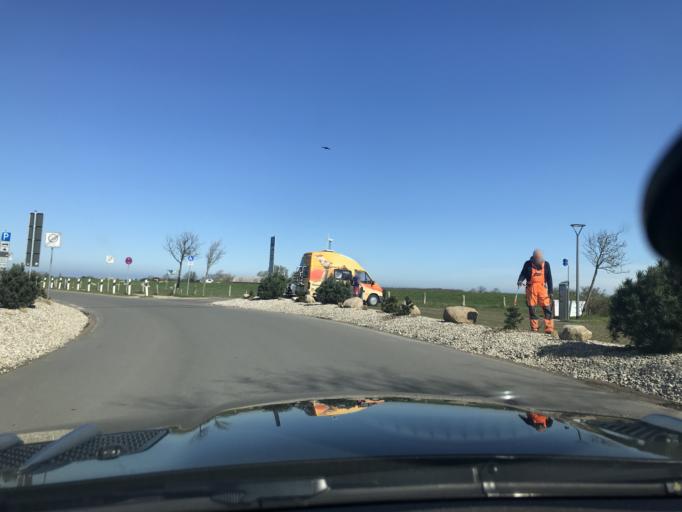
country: DE
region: Schleswig-Holstein
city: Grossenbrode
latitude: 54.4473
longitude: 11.0890
